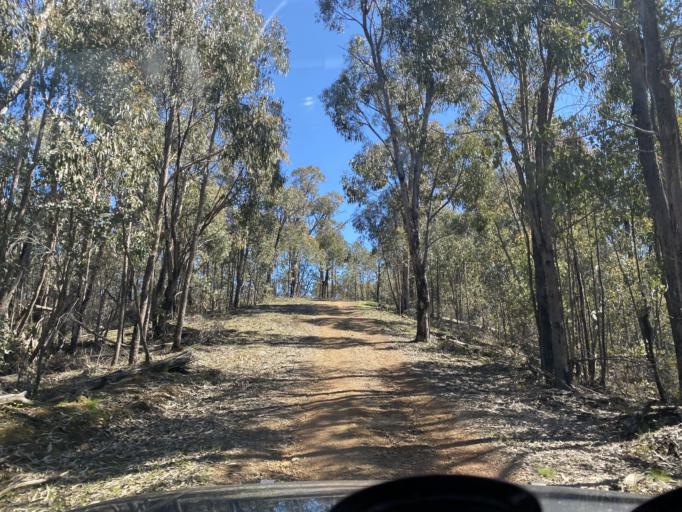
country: AU
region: Victoria
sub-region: Benalla
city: Benalla
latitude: -36.7301
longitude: 146.1821
